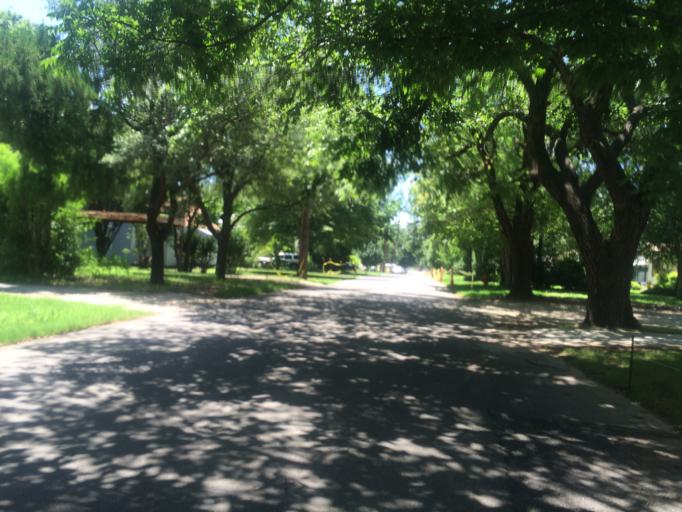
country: US
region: Oklahoma
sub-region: Cleveland County
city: Norman
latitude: 35.2148
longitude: -97.4555
